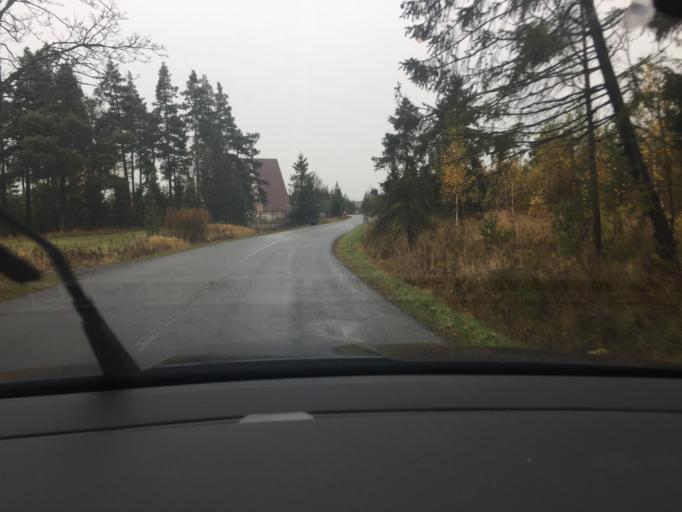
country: SK
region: Presovsky
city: Spisska Bela
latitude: 49.2086
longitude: 20.3727
